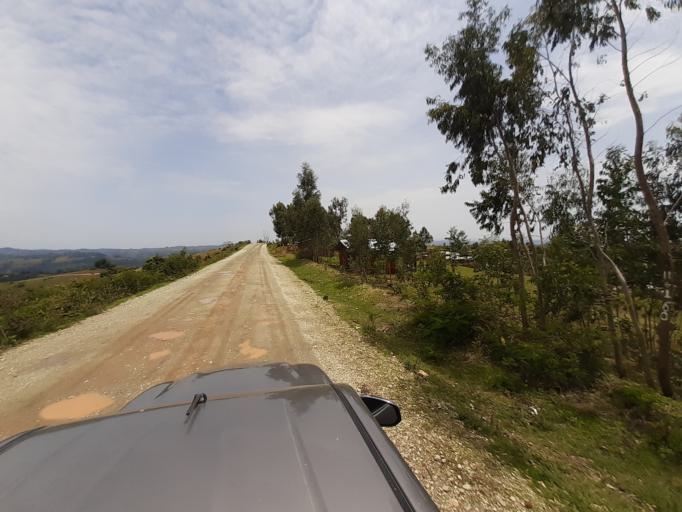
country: ET
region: Oromiya
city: Gimbi
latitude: 9.3525
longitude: 35.6875
